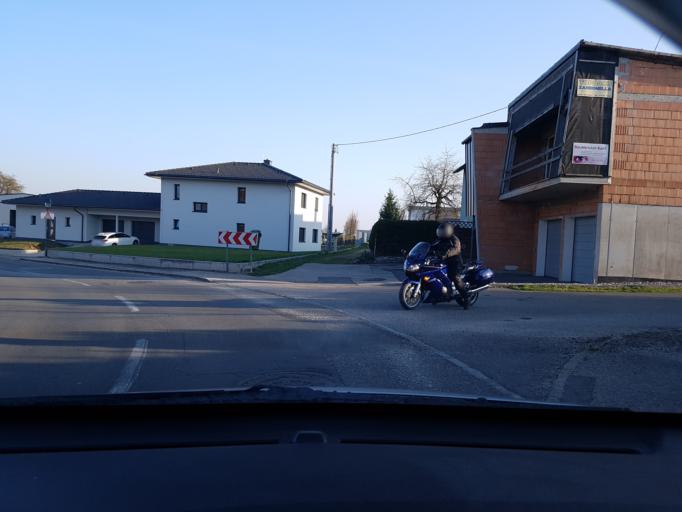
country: AT
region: Upper Austria
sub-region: Politischer Bezirk Linz-Land
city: Ansfelden
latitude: 48.1498
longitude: 14.2743
